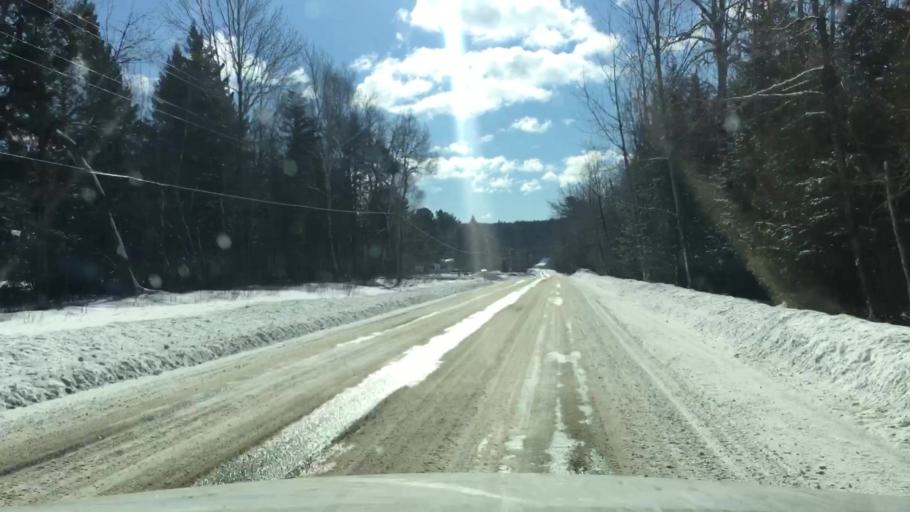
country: US
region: Maine
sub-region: Washington County
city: Calais
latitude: 45.0678
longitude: -67.4740
